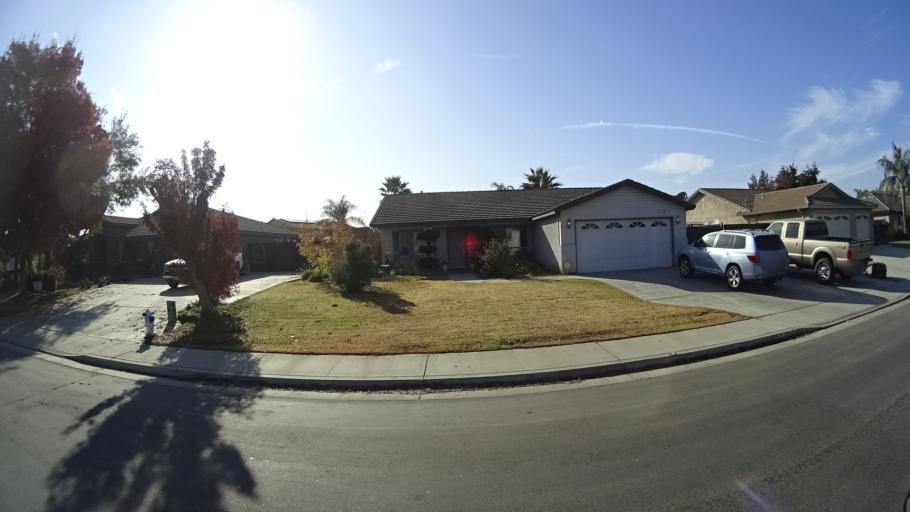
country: US
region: California
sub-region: Kern County
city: Oildale
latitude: 35.4071
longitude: -119.0638
